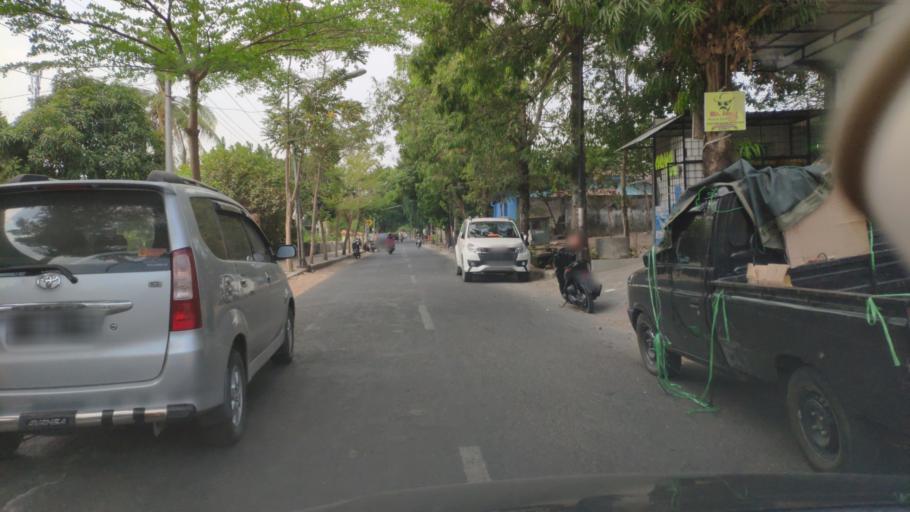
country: ID
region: Central Java
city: Kunden
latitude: -6.9649
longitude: 111.4130
